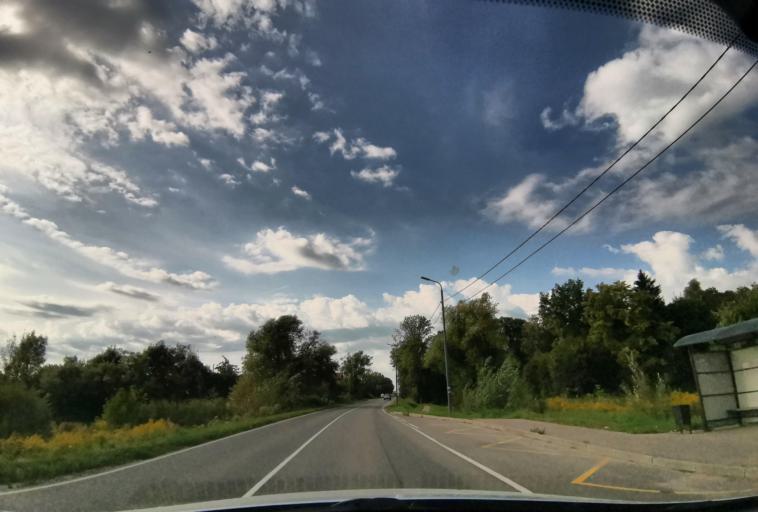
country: RU
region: Kaliningrad
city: Neman
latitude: 55.0263
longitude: 22.0561
